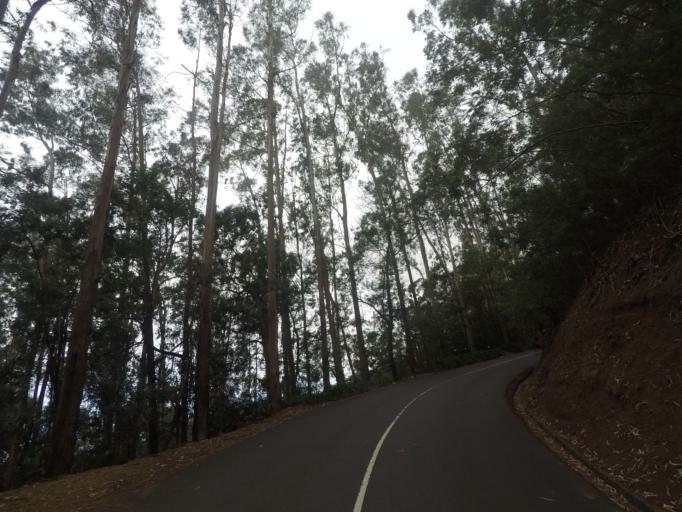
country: PT
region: Madeira
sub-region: Funchal
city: Nossa Senhora do Monte
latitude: 32.6664
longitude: -16.8756
